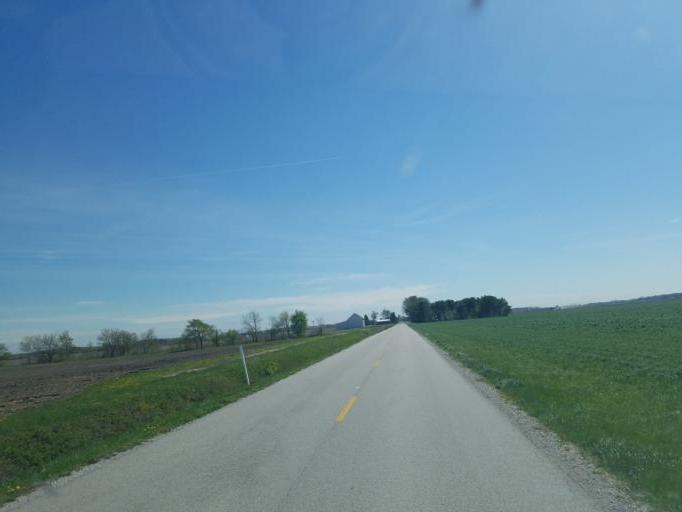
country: US
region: Ohio
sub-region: Huron County
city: Bellevue
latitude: 41.3178
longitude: -82.7929
